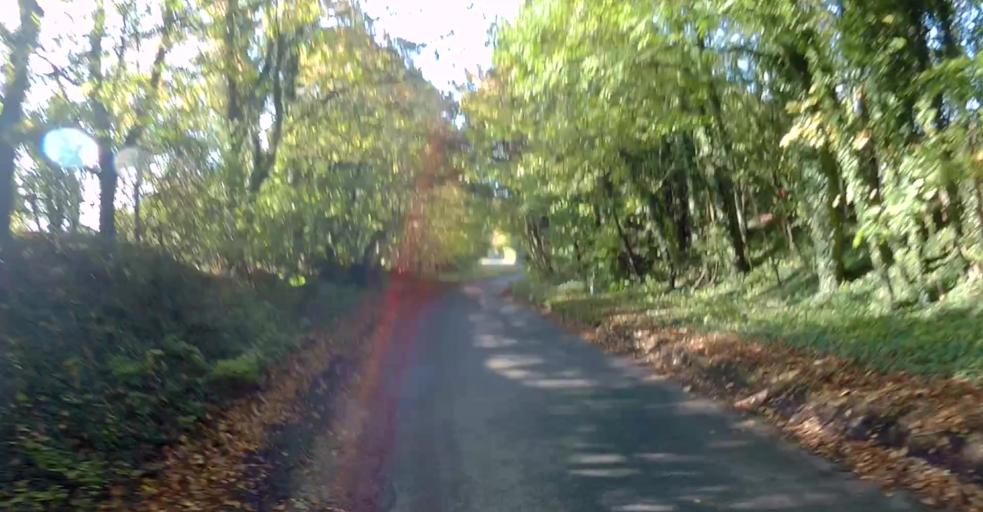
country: GB
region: England
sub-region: Hampshire
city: Long Sutton
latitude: 51.2150
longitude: -0.9187
